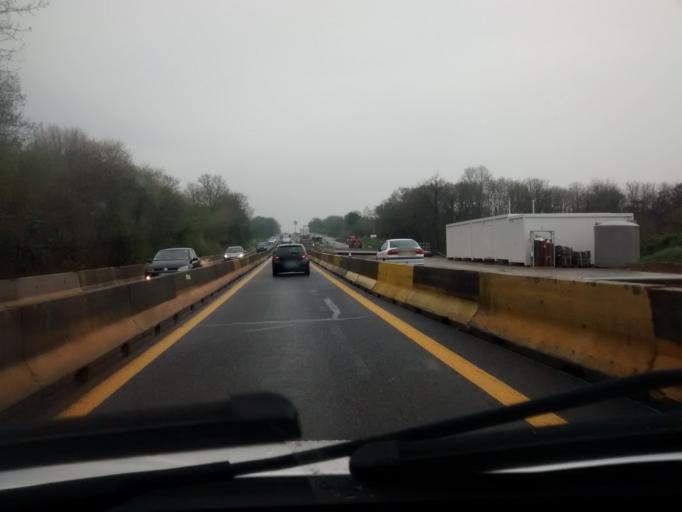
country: FR
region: Brittany
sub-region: Departement des Cotes-d'Armor
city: Plelo
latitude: 48.5307
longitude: -2.9543
